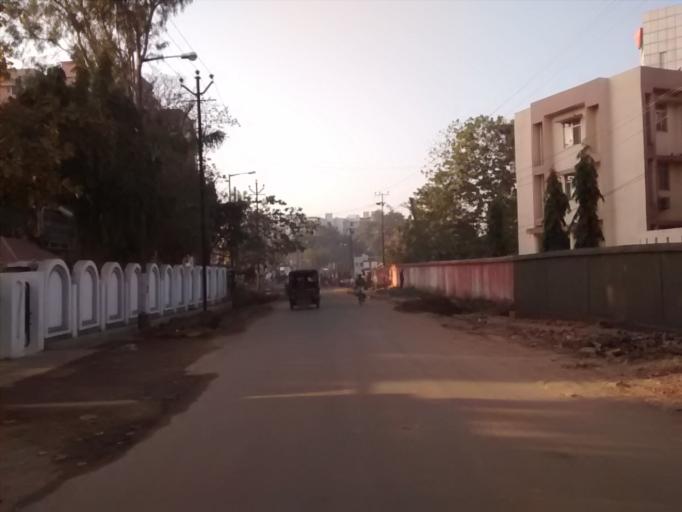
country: IN
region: Jharkhand
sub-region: Ranchi
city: Ranchi
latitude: 23.3746
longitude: 85.3274
